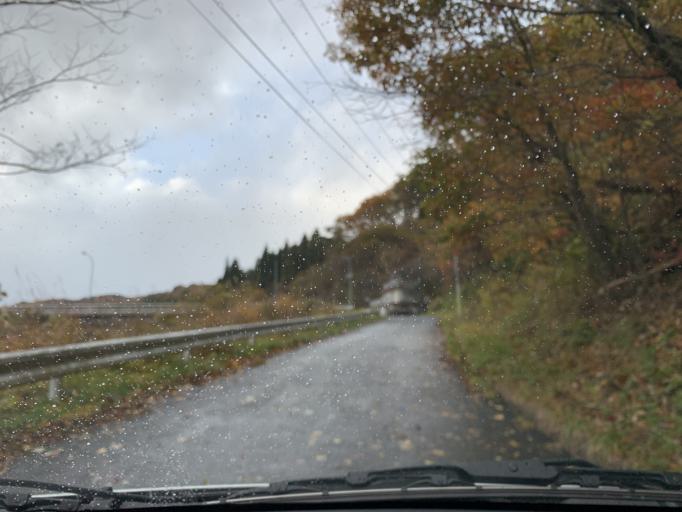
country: JP
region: Iwate
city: Mizusawa
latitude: 39.1005
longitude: 140.9675
